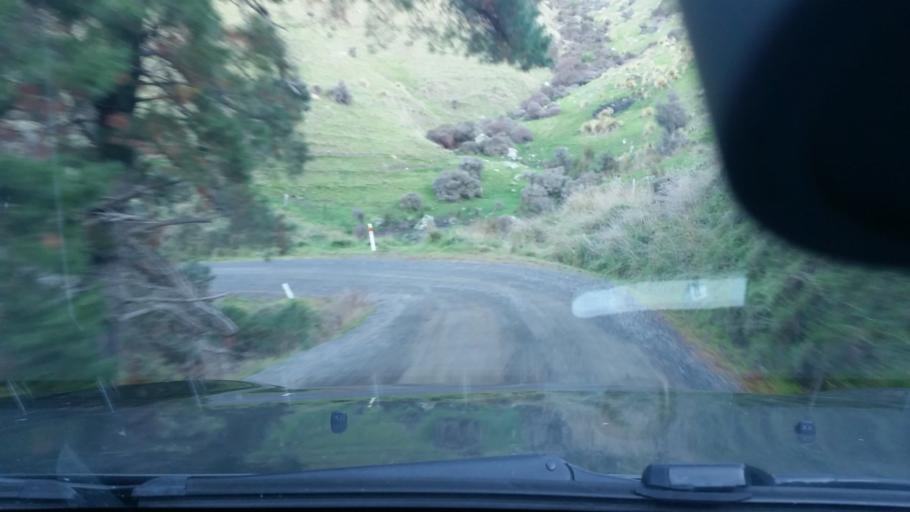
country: NZ
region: Marlborough
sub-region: Marlborough District
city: Blenheim
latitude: -41.7502
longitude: 174.0592
